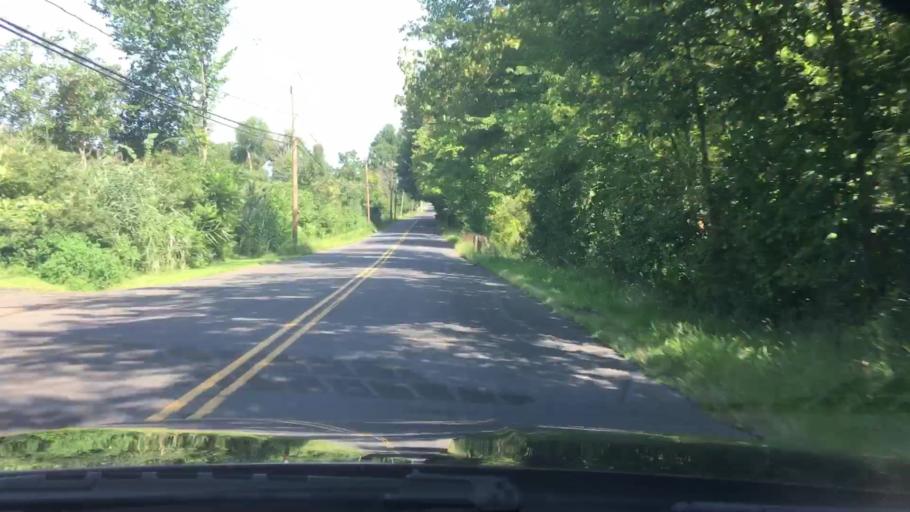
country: US
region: Connecticut
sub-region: Hartford County
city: Kensington
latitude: 41.6110
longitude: -72.7647
